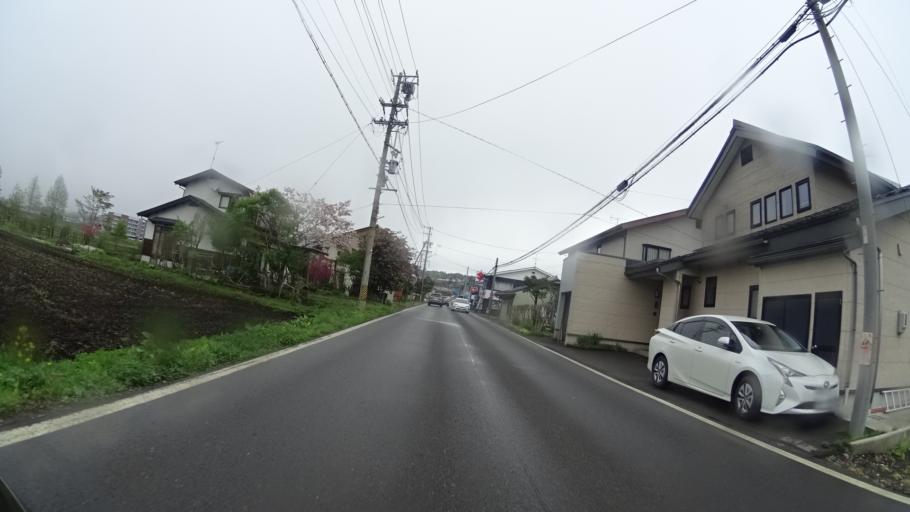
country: JP
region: Nagano
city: Nagano-shi
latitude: 36.8034
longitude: 138.1954
